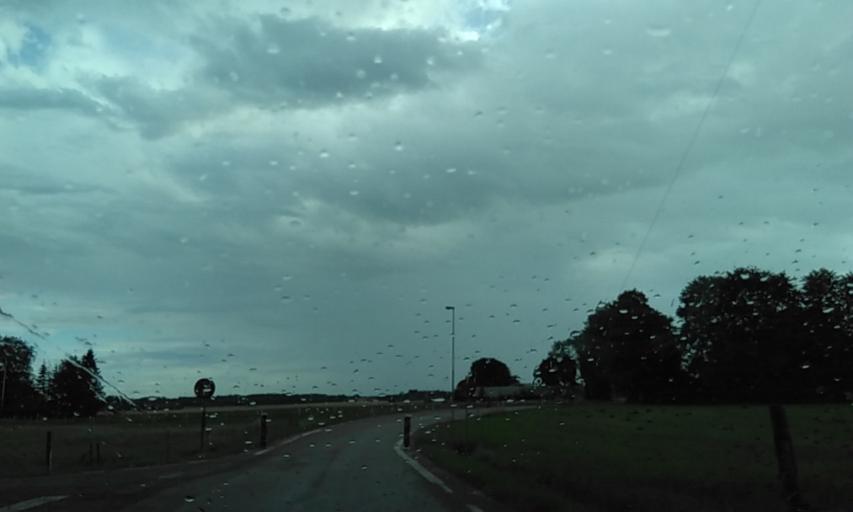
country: SE
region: Vaestra Goetaland
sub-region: Grastorps Kommun
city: Graestorp
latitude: 58.4499
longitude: 12.7782
